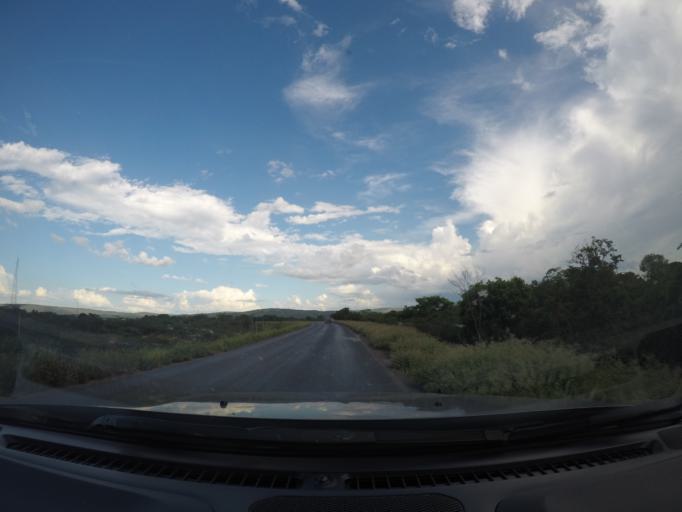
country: BR
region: Bahia
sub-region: Ibotirama
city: Ibotirama
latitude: -12.1816
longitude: -43.2358
